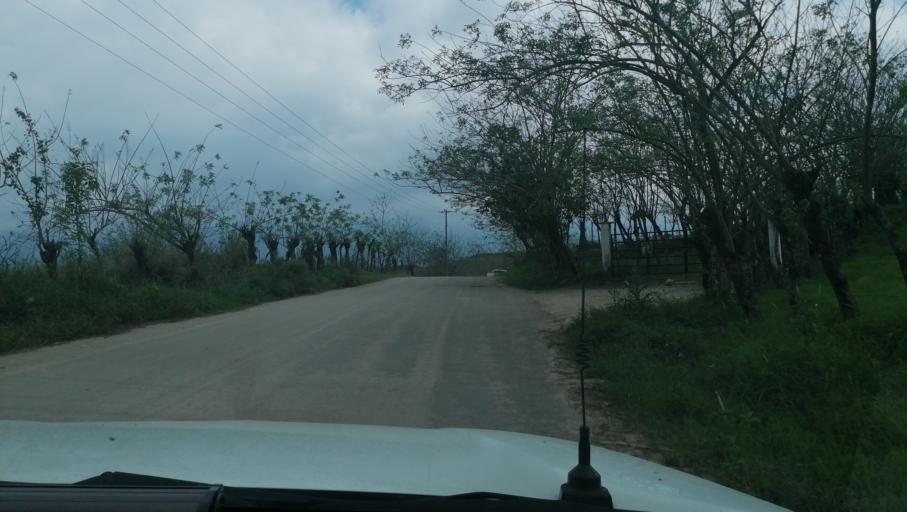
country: MX
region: Chiapas
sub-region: Francisco Leon
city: San Miguel la Sardina
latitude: 17.2704
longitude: -93.2638
